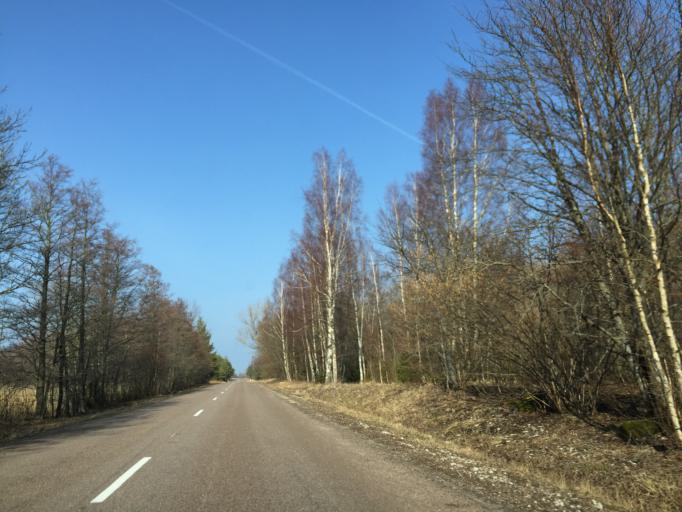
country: LV
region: Dundaga
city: Dundaga
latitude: 57.9634
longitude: 21.9983
